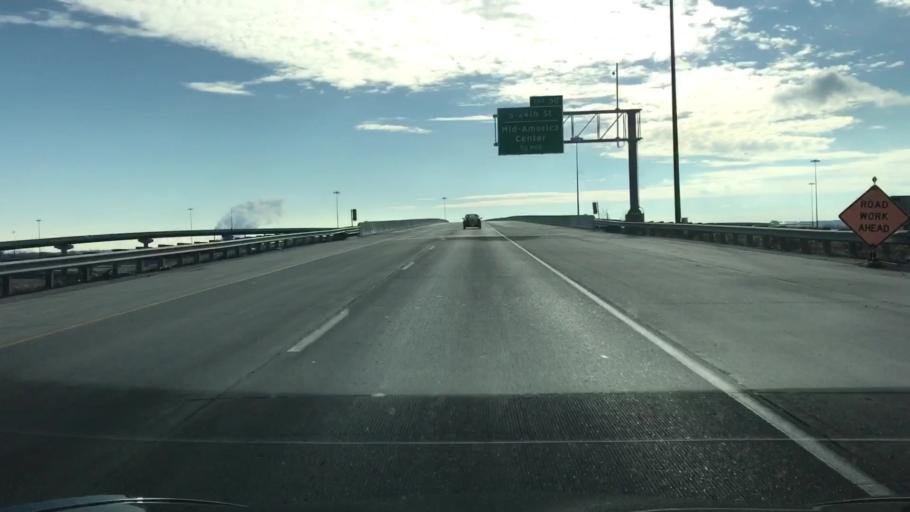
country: US
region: Nebraska
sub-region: Douglas County
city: Omaha
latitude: 41.2367
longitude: -95.9006
